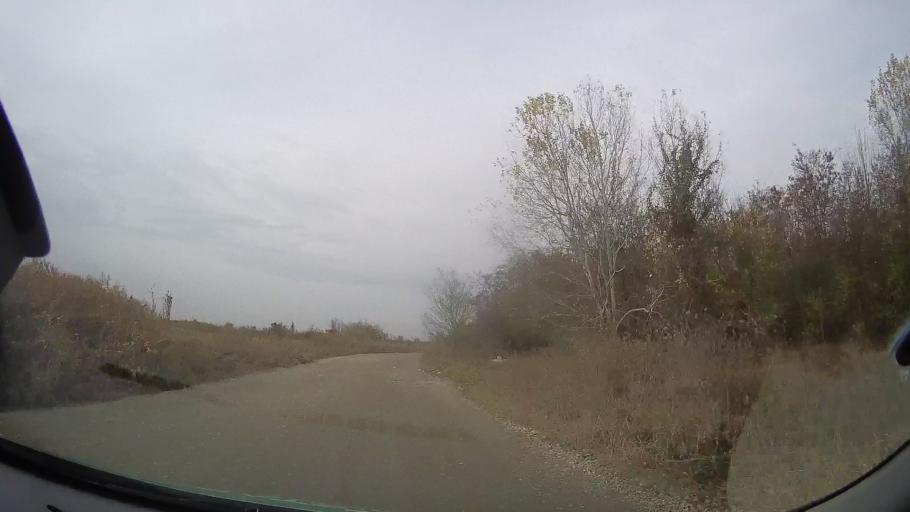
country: RO
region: Ialomita
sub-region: Comuna Fierbinti-Targ
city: Fierbinti-Targ
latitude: 44.6786
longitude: 26.3478
